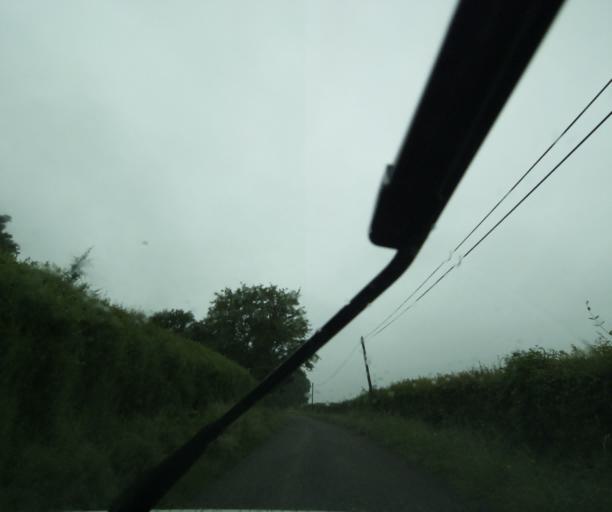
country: FR
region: Bourgogne
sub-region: Departement de Saone-et-Loire
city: Charolles
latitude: 46.4044
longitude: 4.2920
